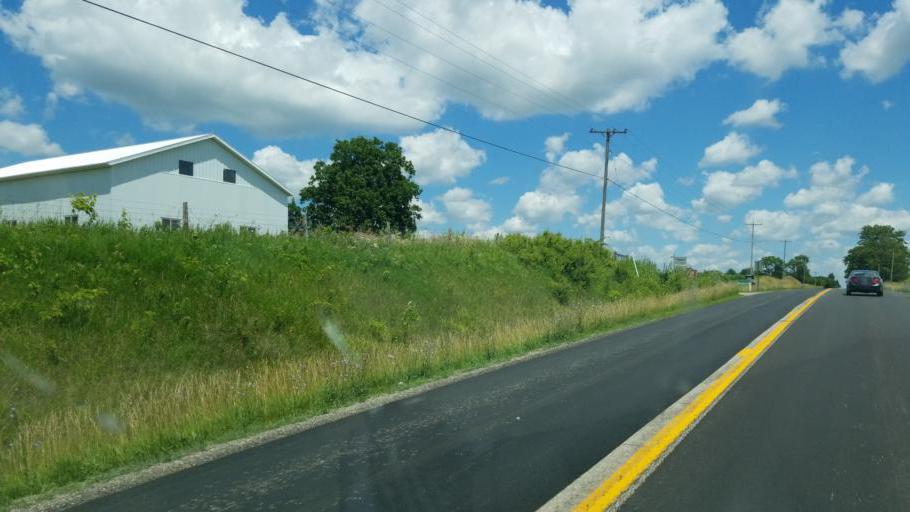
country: US
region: Ohio
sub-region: Richland County
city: Lexington
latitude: 40.6076
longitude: -82.6625
